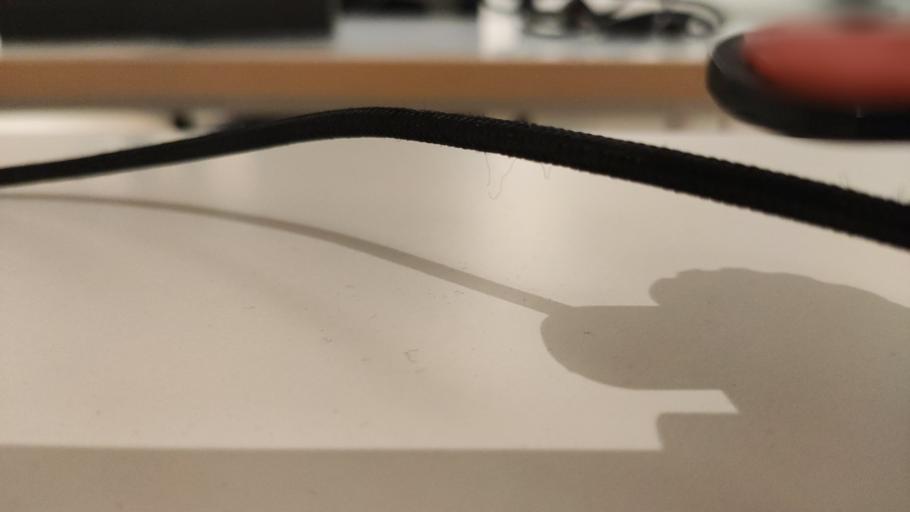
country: RU
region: Moskovskaya
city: Dorokhovo
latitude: 55.5246
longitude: 36.3542
